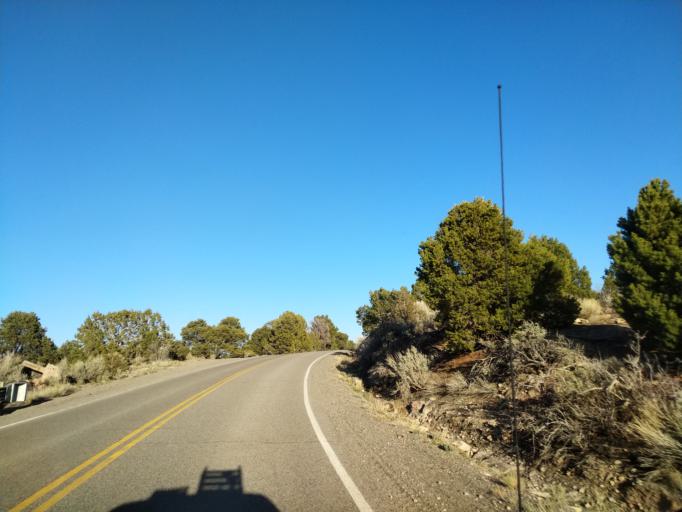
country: US
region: Colorado
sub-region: Mesa County
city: Redlands
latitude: 38.9923
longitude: -108.7715
